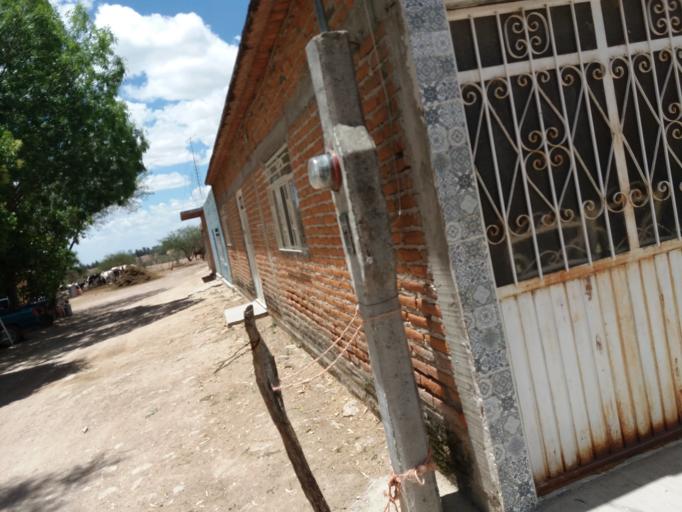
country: MX
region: Aguascalientes
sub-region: Aguascalientes
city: San Sebastian [Fraccionamiento]
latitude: 21.7789
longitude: -102.2632
